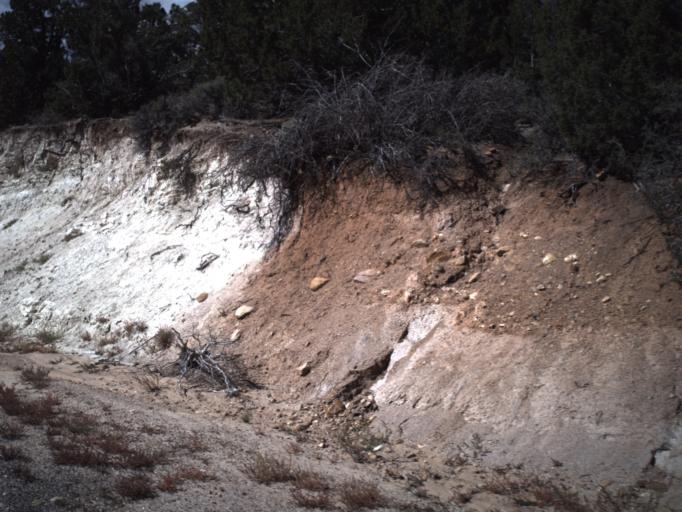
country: US
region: Utah
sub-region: Washington County
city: Enterprise
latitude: 37.5411
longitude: -113.6776
